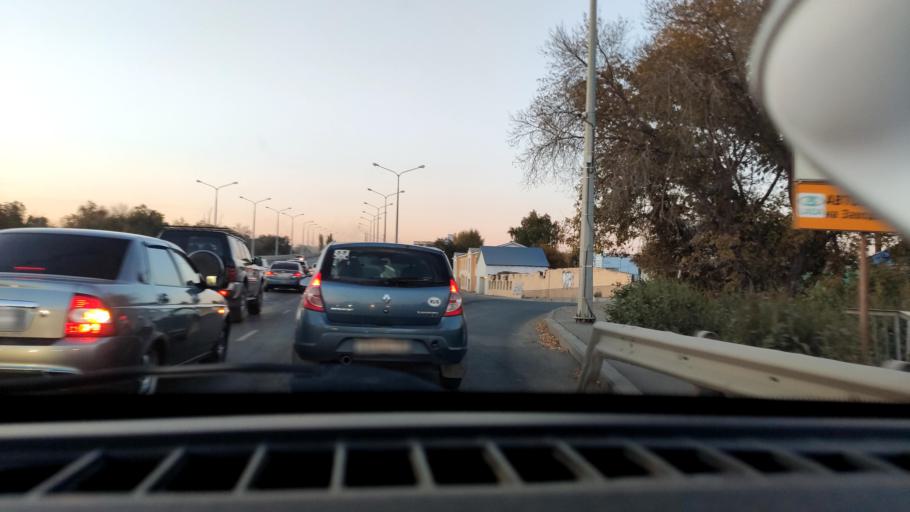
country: RU
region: Samara
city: Samara
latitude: 53.1711
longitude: 50.1950
